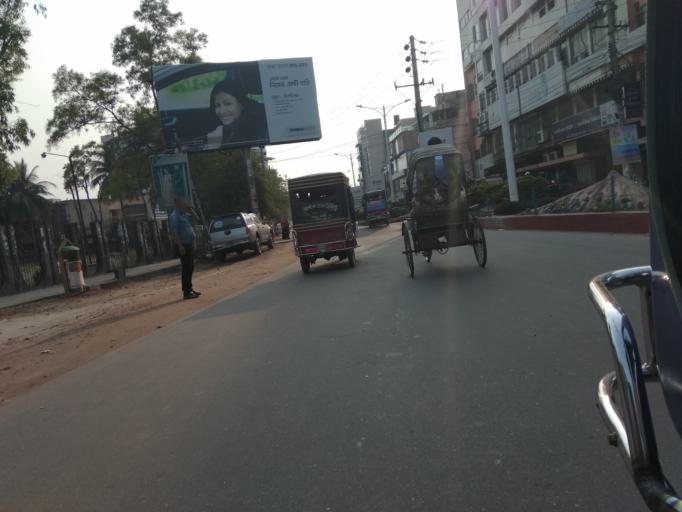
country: BD
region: Khulna
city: Khulna
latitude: 22.8220
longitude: 89.5524
